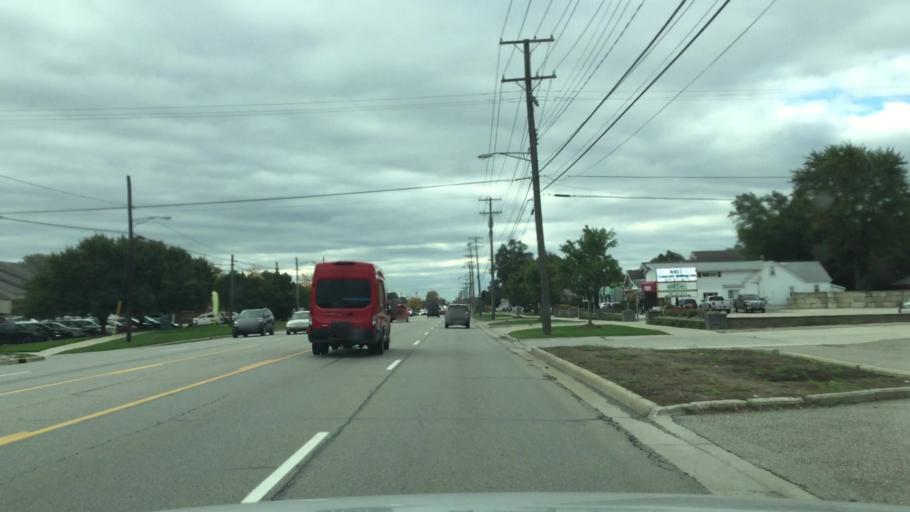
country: US
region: Michigan
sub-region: Macomb County
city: Utica
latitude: 42.6474
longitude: -83.0333
